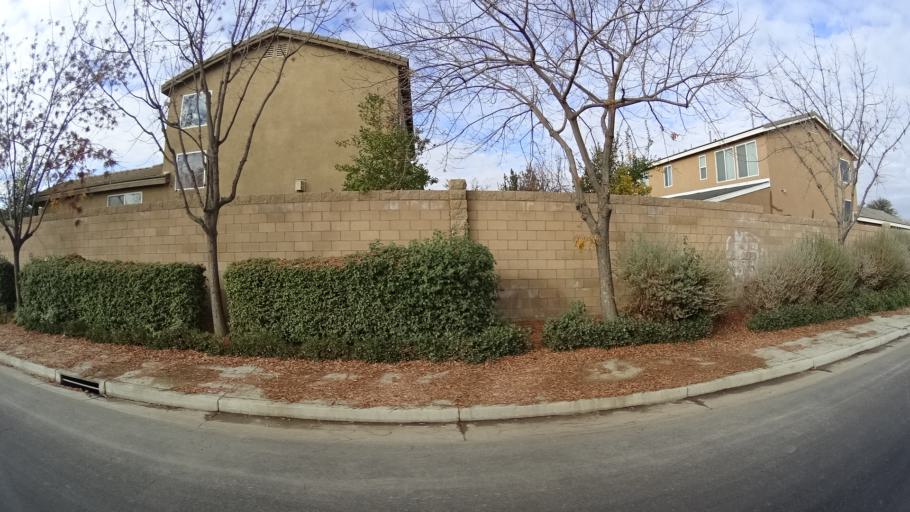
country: US
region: California
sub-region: Kern County
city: Rosedale
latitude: 35.2989
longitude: -119.1371
